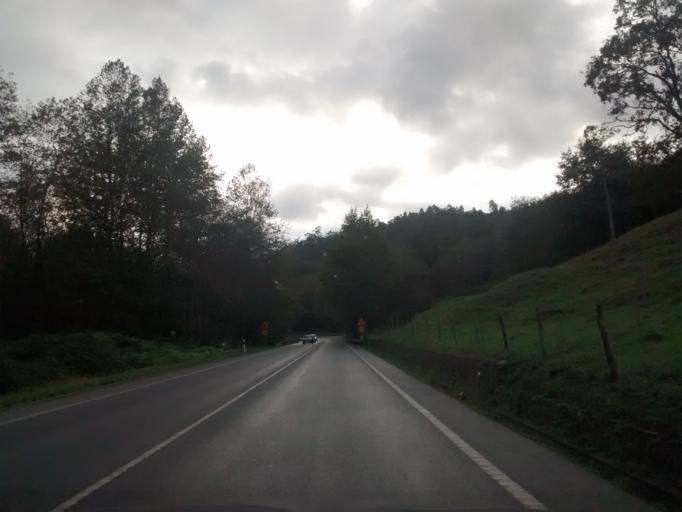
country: ES
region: Cantabria
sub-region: Provincia de Cantabria
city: Penagos
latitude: 43.3509
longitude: -3.7833
